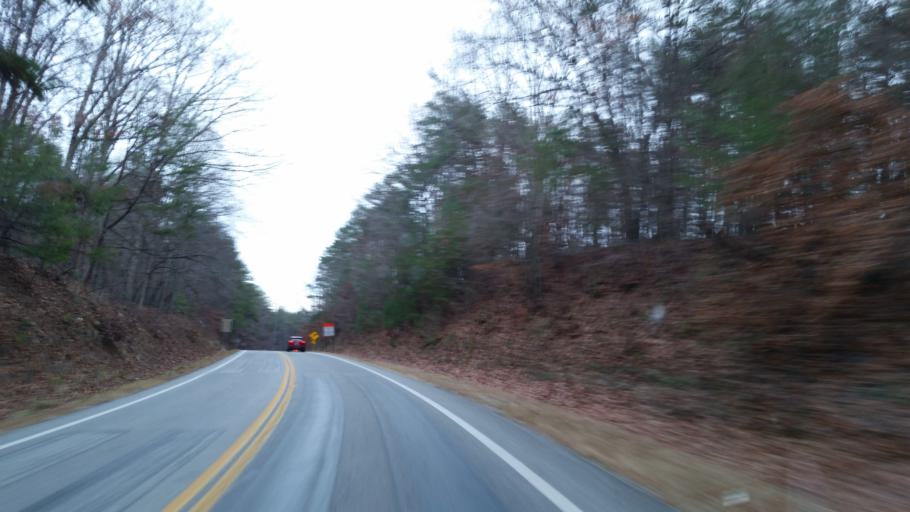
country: US
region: Georgia
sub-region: Dawson County
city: Dawsonville
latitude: 34.4134
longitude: -84.0270
